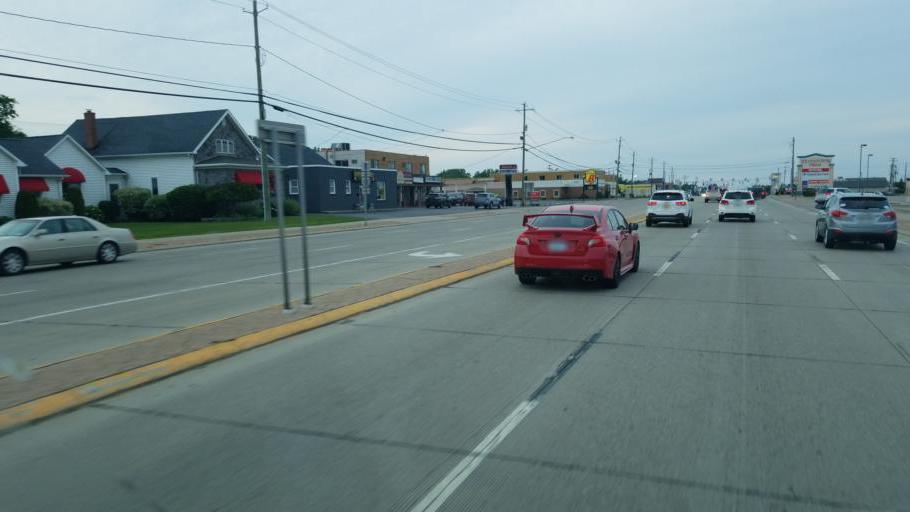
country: US
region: New York
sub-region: Erie County
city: Harris Hill
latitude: 42.9622
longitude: -78.6968
